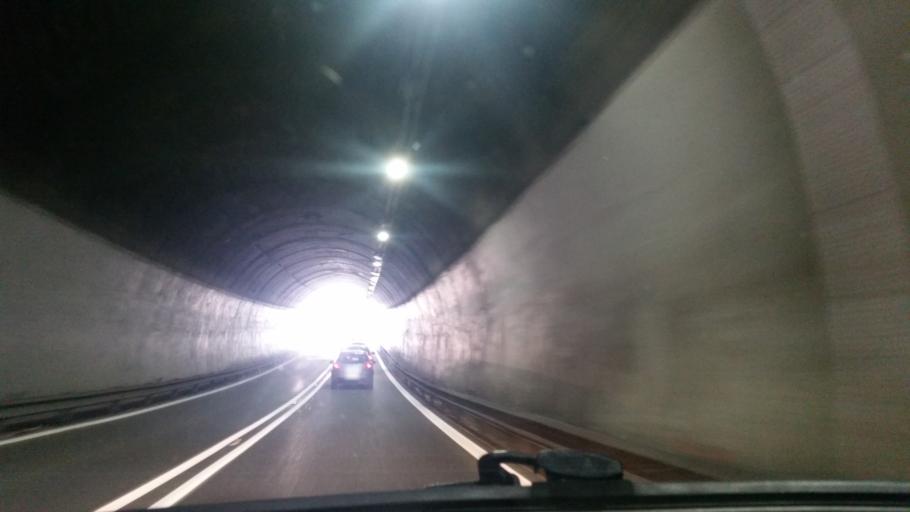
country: IT
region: Campania
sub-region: Provincia di Napoli
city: Napoli
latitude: 40.8572
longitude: 14.2326
